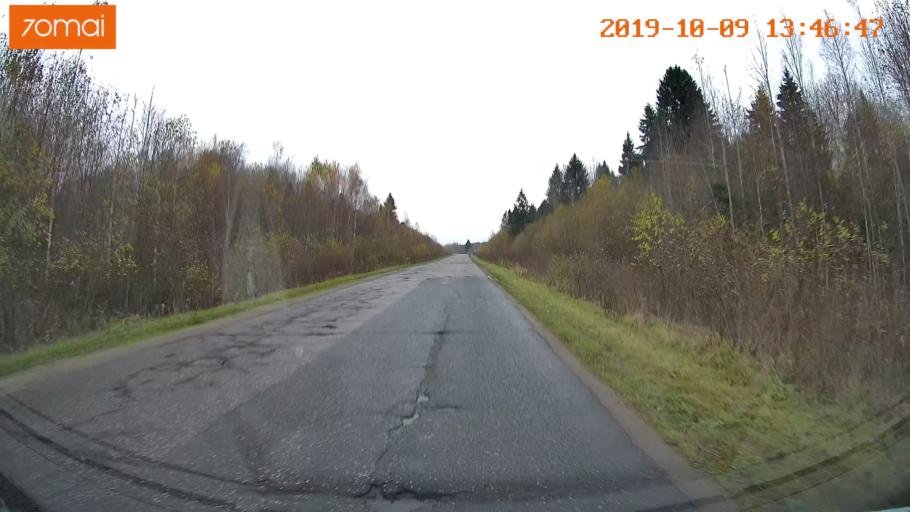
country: RU
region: Kostroma
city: Buy
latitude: 58.3861
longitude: 41.2200
